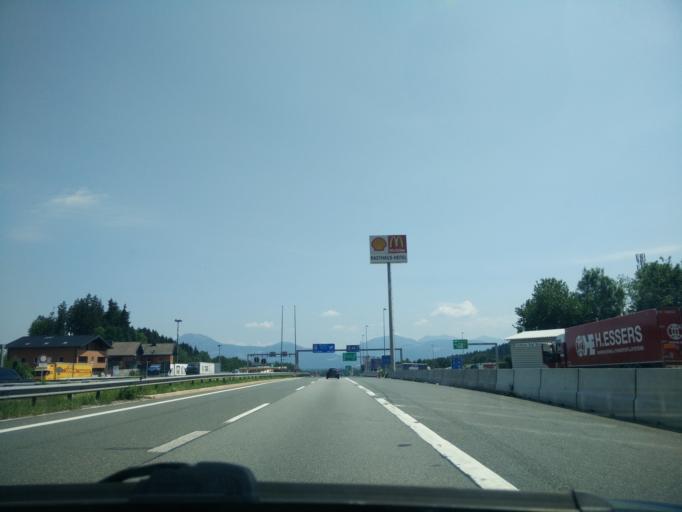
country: DE
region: Bavaria
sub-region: Upper Bavaria
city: Piding
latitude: 47.7682
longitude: 12.9423
